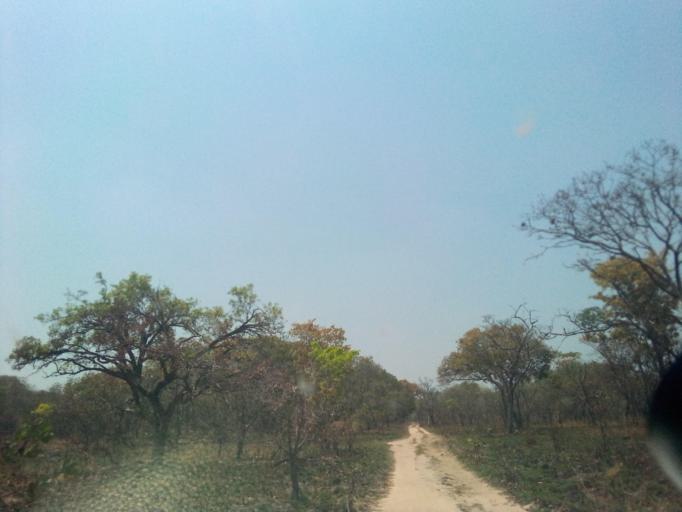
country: ZM
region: Copperbelt
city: Kataba
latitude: -12.2417
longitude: 30.4012
